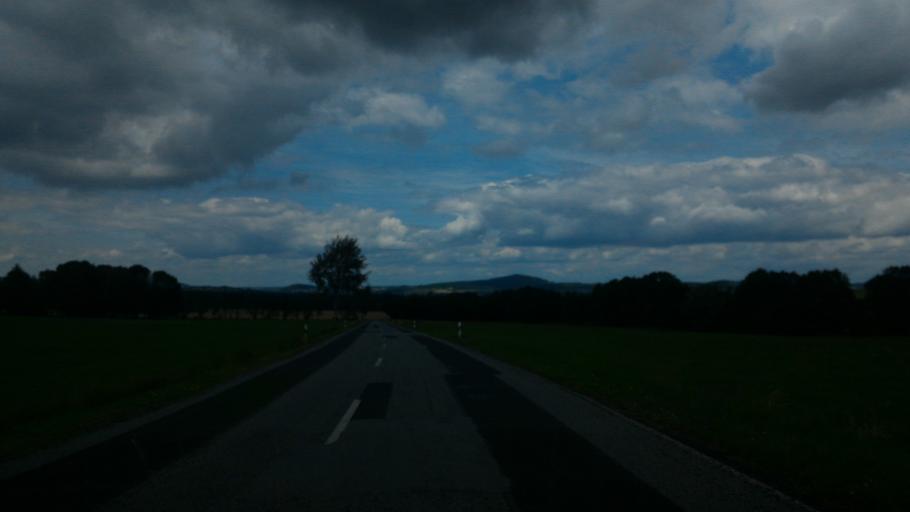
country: DE
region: Saxony
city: Kurort Jonsdorf
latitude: 50.8630
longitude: 14.6935
